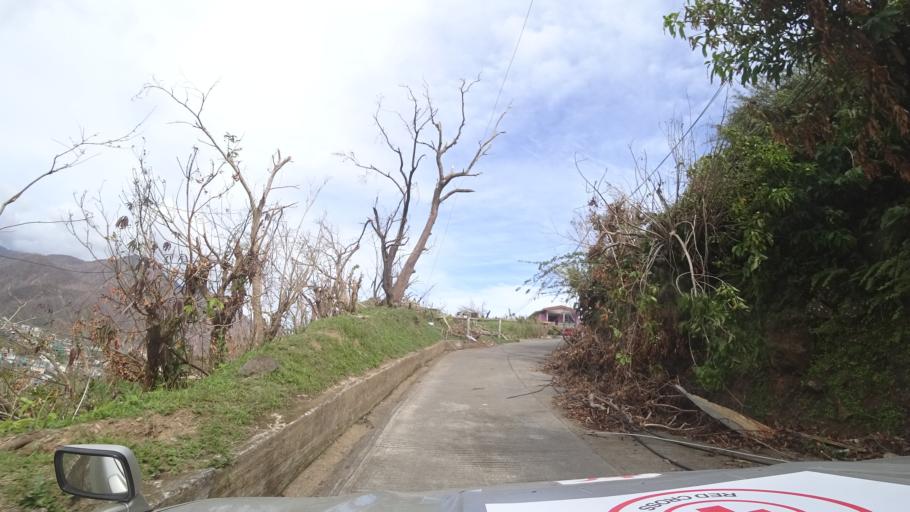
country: DM
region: Saint Patrick
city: Berekua
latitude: 15.2368
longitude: -61.3249
